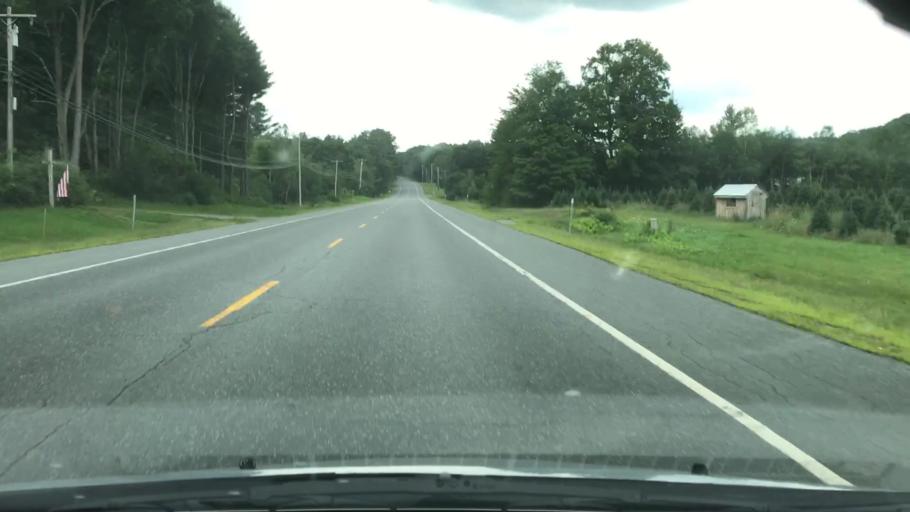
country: US
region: New Hampshire
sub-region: Grafton County
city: Lyme
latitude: 43.7911
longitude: -72.1725
